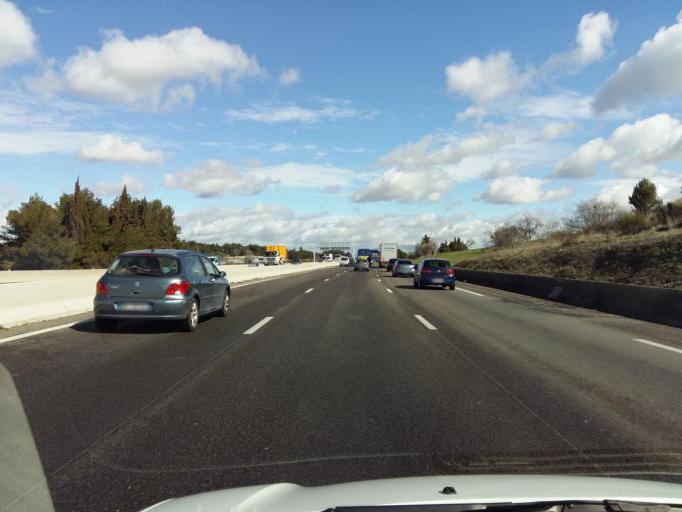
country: FR
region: Provence-Alpes-Cote d'Azur
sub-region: Departement des Bouches-du-Rhone
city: Septemes-les-Vallons
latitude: 43.4206
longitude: 5.3690
